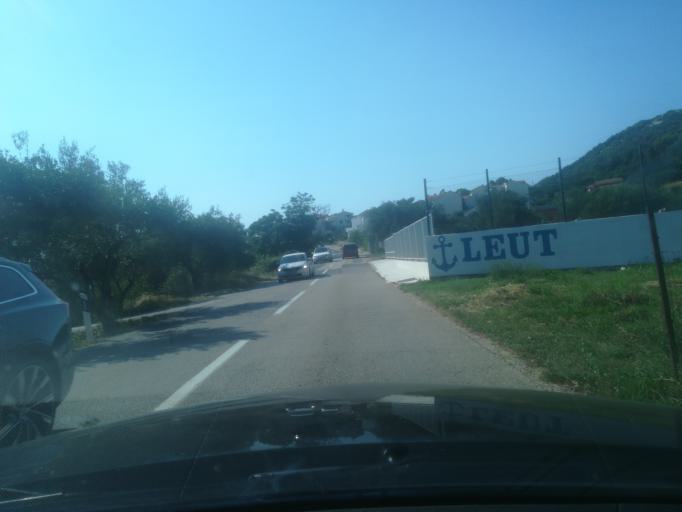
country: HR
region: Primorsko-Goranska
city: Banjol
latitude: 44.7335
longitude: 14.8094
